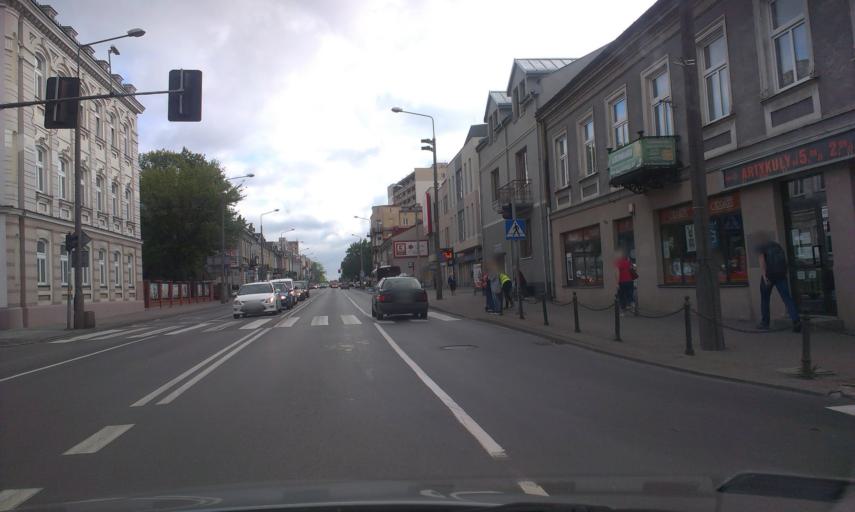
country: PL
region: Masovian Voivodeship
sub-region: Radom
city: Radom
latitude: 51.3978
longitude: 21.1616
